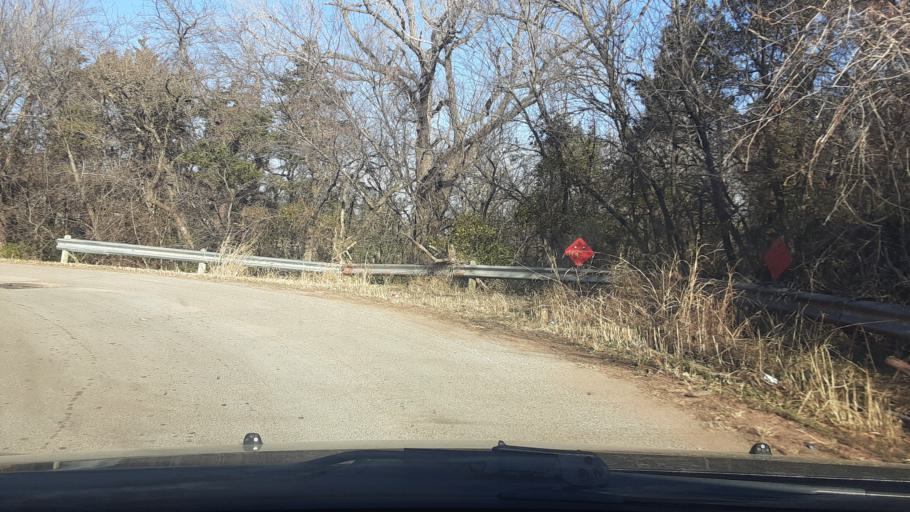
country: US
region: Oklahoma
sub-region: Logan County
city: Guthrie
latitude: 35.8769
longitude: -97.4025
